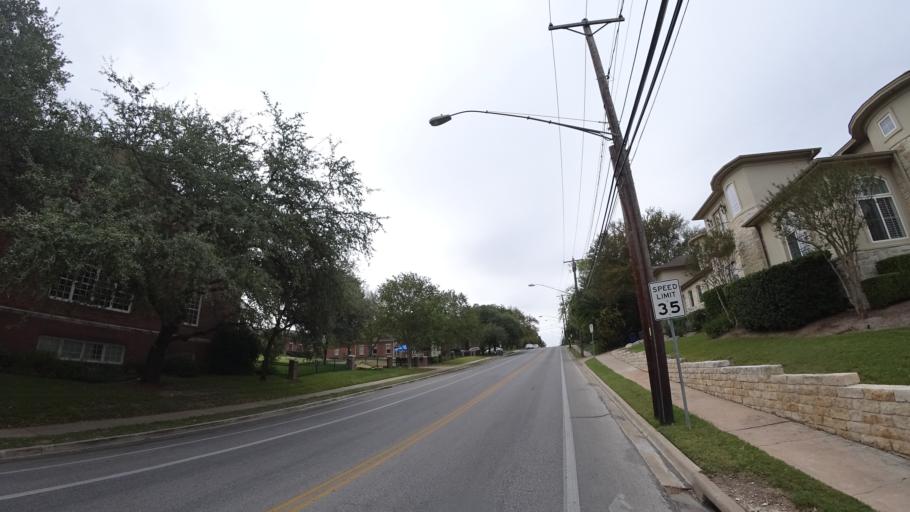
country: US
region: Texas
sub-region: Travis County
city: Rollingwood
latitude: 30.3012
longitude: -97.7654
